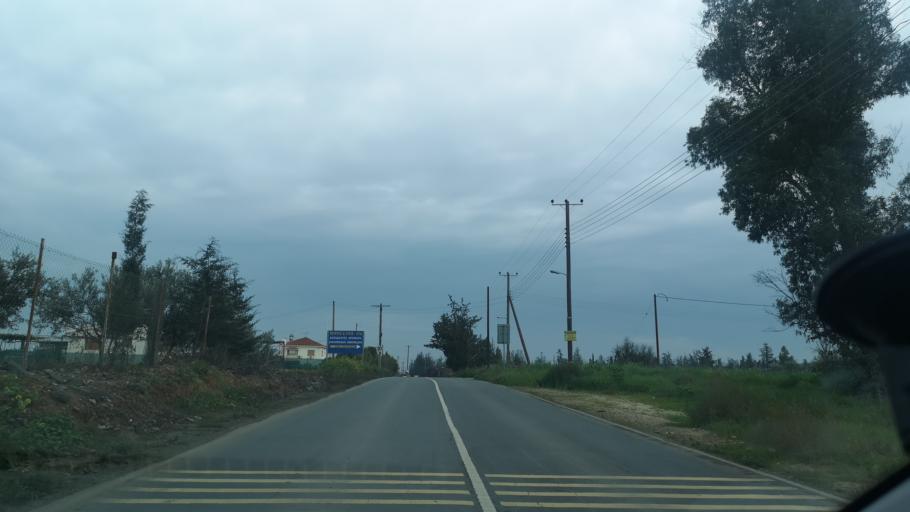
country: CY
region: Lefkosia
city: Kato Deftera
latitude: 35.0837
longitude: 33.2968
